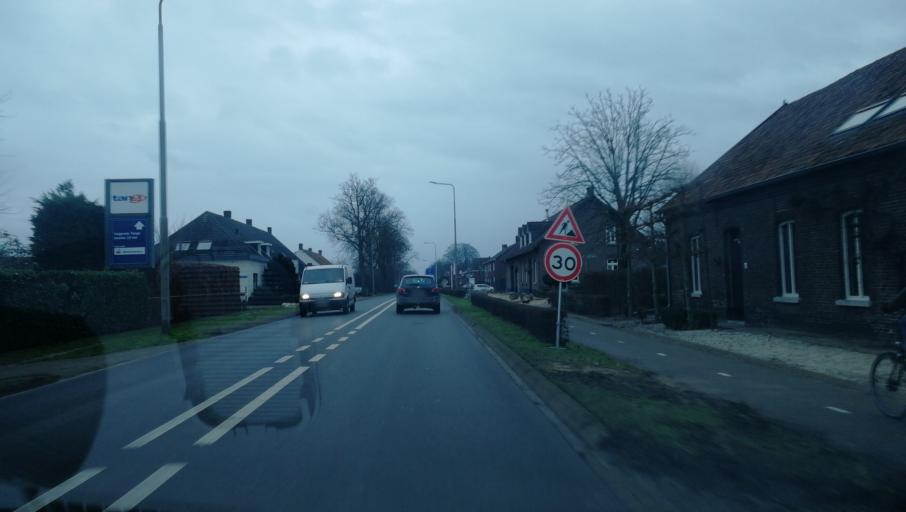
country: NL
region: Limburg
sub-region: Gemeente Venlo
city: Tegelen
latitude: 51.3346
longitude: 6.0950
